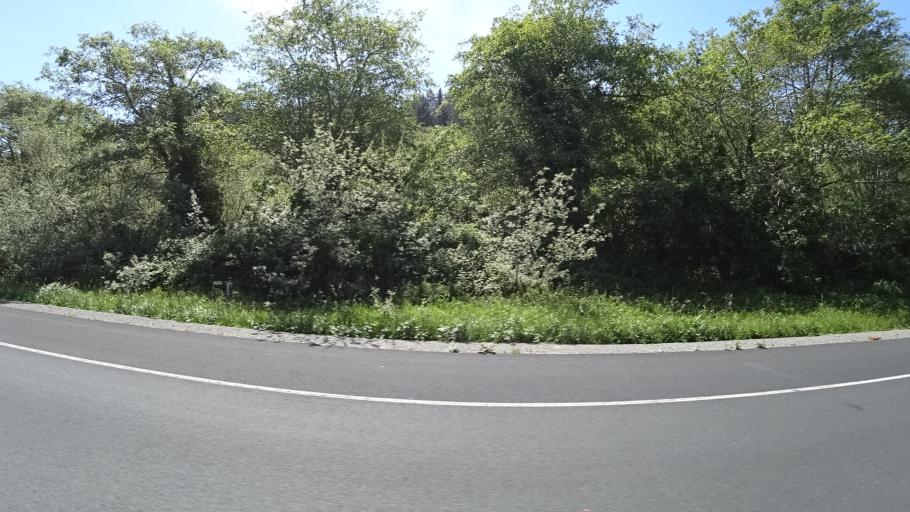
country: US
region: California
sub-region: Humboldt County
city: Westhaven-Moonstone
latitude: 41.2872
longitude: -124.0841
